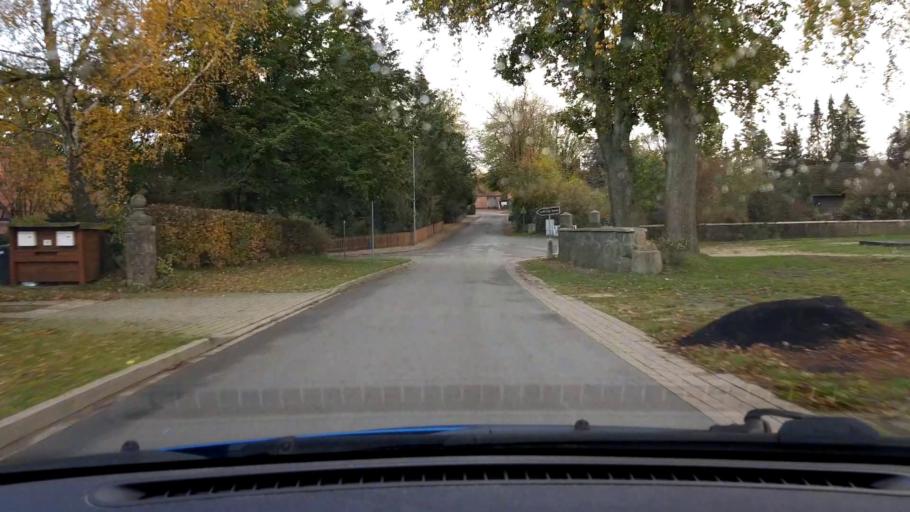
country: DE
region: Lower Saxony
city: Reinstorf
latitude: 53.2428
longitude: 10.5809
